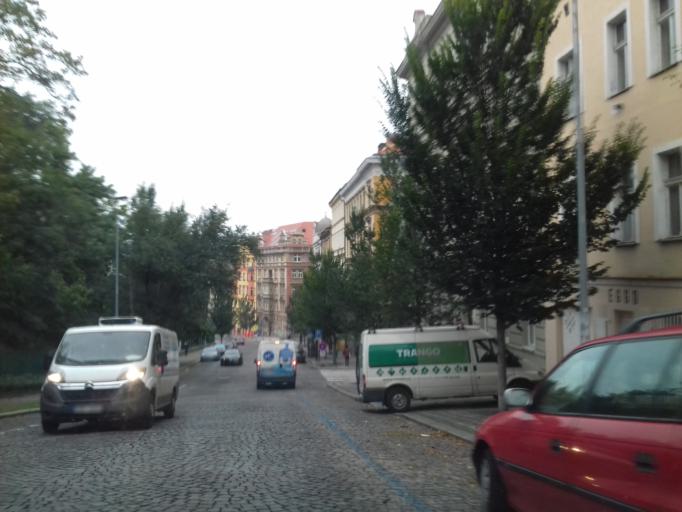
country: CZ
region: Praha
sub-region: Praha 8
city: Karlin
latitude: 50.0816
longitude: 14.4446
